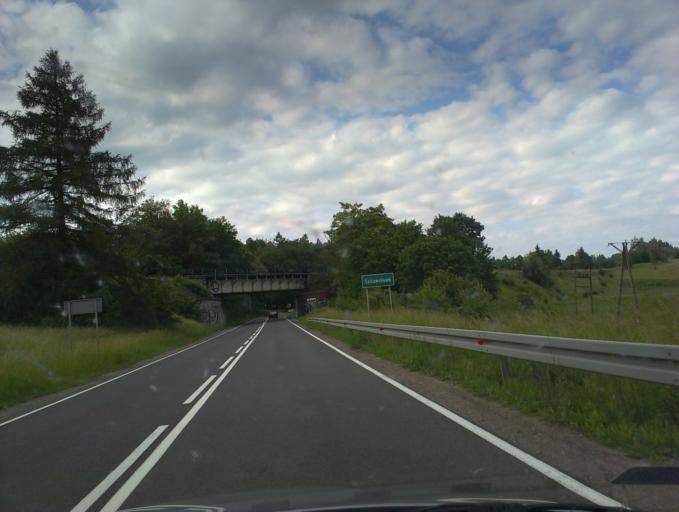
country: PL
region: West Pomeranian Voivodeship
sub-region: Powiat szczecinecki
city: Szczecinek
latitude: 53.6830
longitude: 16.6885
